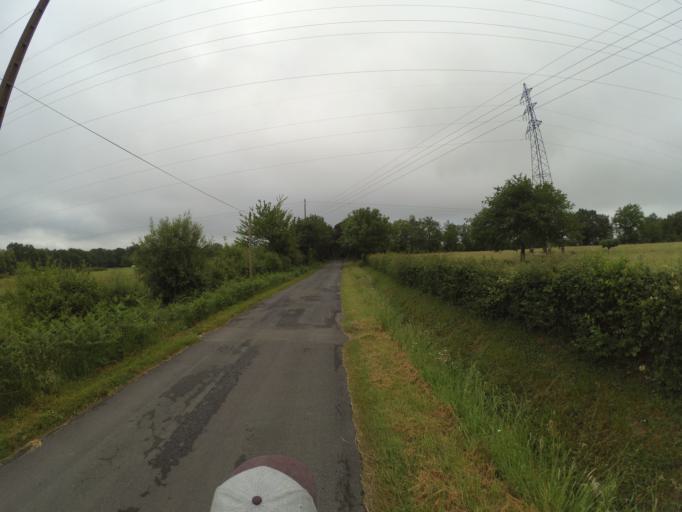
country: FR
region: Pays de la Loire
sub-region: Departement de la Vendee
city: La Roche-sur-Yon
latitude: 46.6331
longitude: -1.4267
